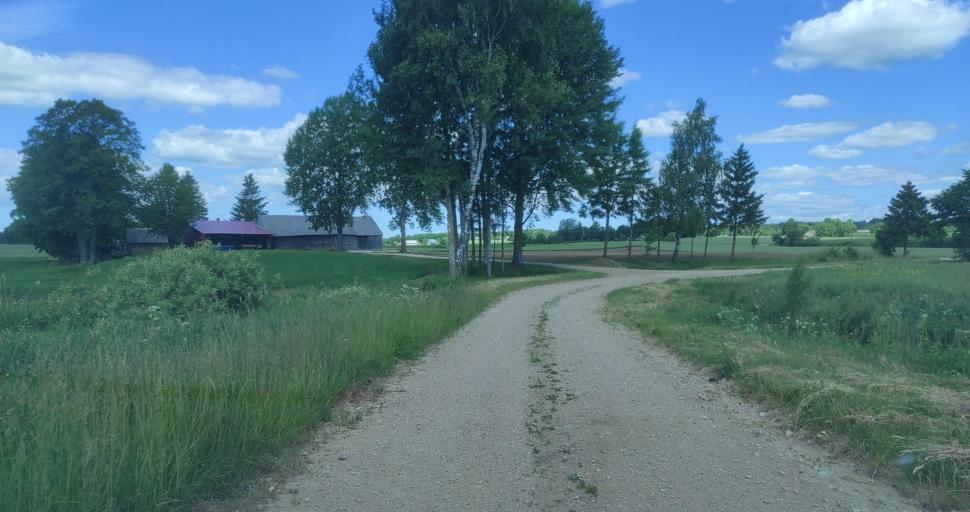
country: LV
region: Aizpute
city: Aizpute
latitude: 56.8657
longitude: 21.6973
